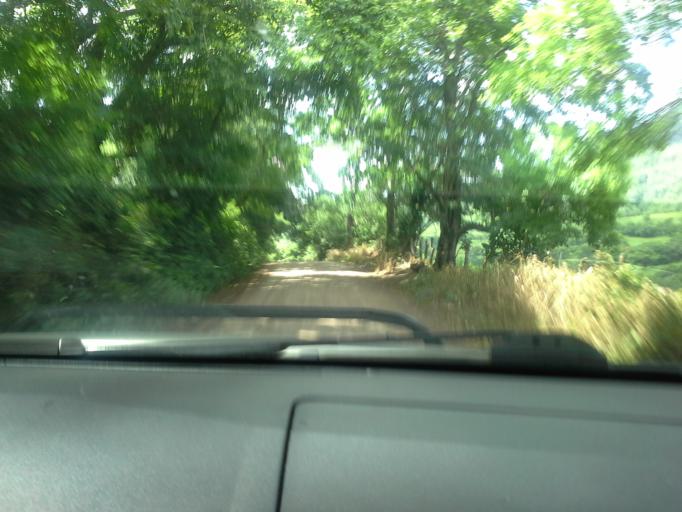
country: NI
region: Matagalpa
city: Terrabona
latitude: 12.7159
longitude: -85.9628
